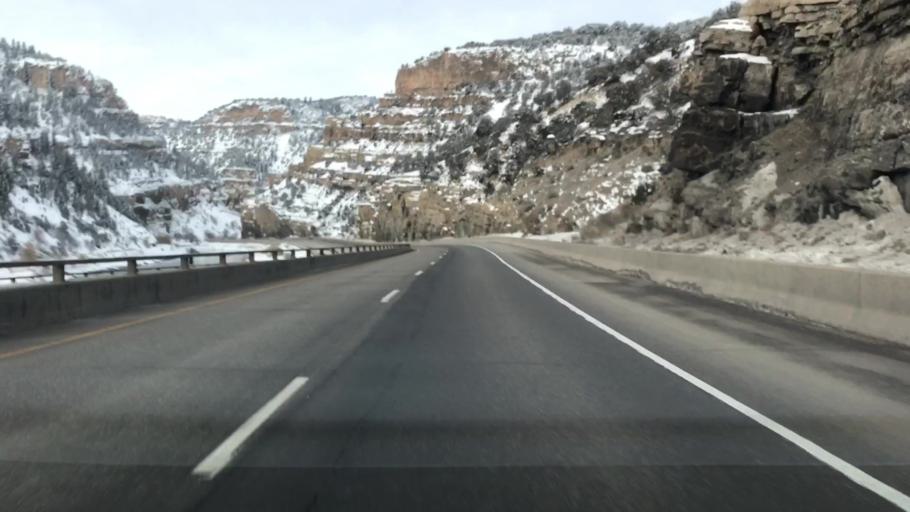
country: US
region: Colorado
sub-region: Eagle County
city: Gypsum
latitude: 39.6257
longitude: -107.1073
